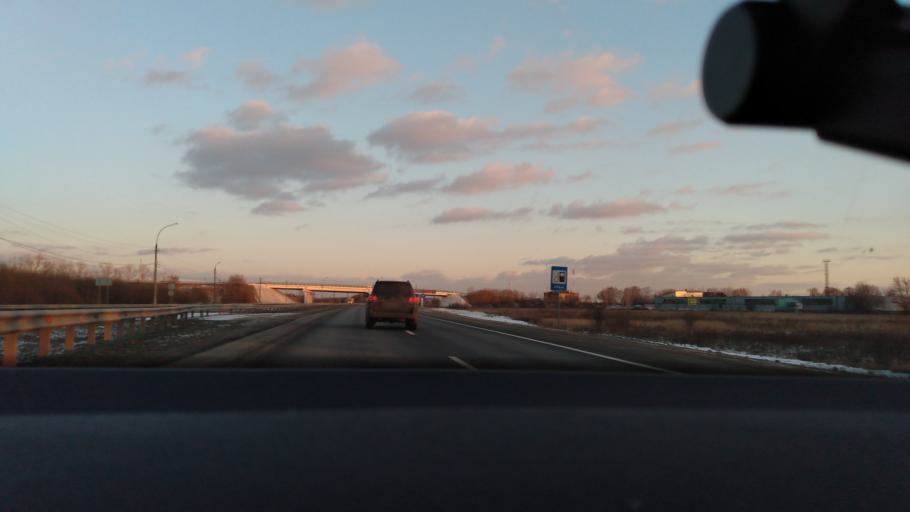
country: RU
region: Moskovskaya
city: Raduzhnyy
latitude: 55.1469
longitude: 38.7248
